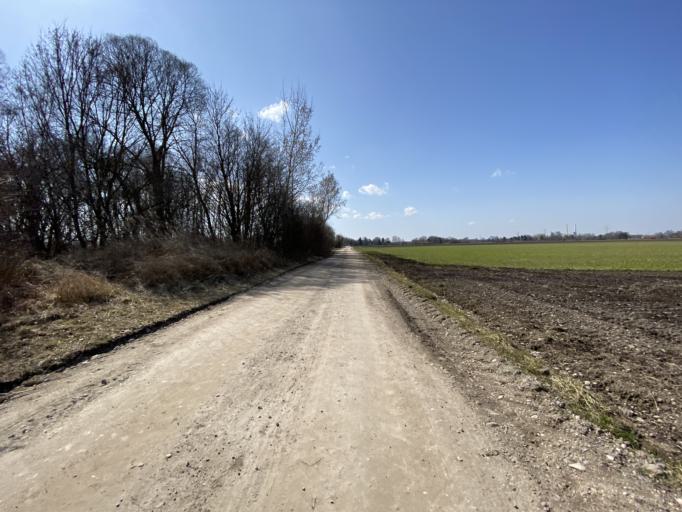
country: DE
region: Bavaria
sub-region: Upper Bavaria
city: Aschheim
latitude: 48.1748
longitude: 11.6806
